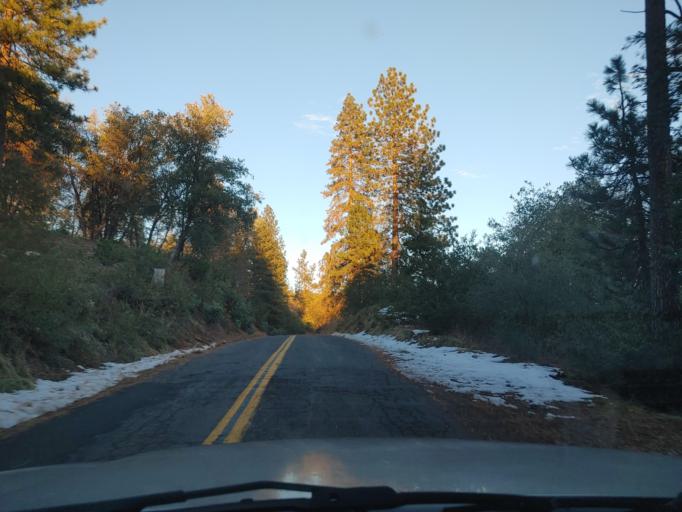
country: US
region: California
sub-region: Tuolumne County
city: Cedar Ridge
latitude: 38.0399
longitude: -120.3054
